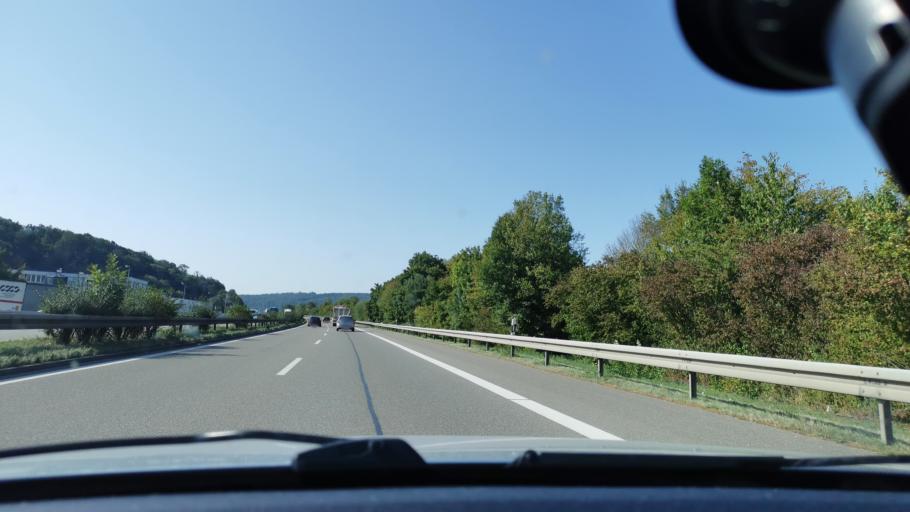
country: DE
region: Baden-Wuerttemberg
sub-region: Regierungsbezirk Stuttgart
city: Uhingen
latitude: 48.7077
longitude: 9.5740
